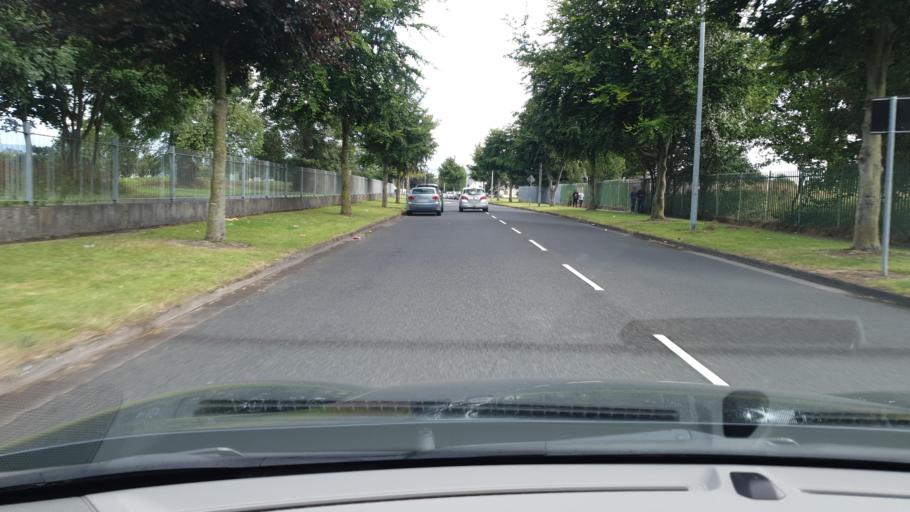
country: IE
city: Cherry Orchard
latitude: 53.3413
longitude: -6.3942
